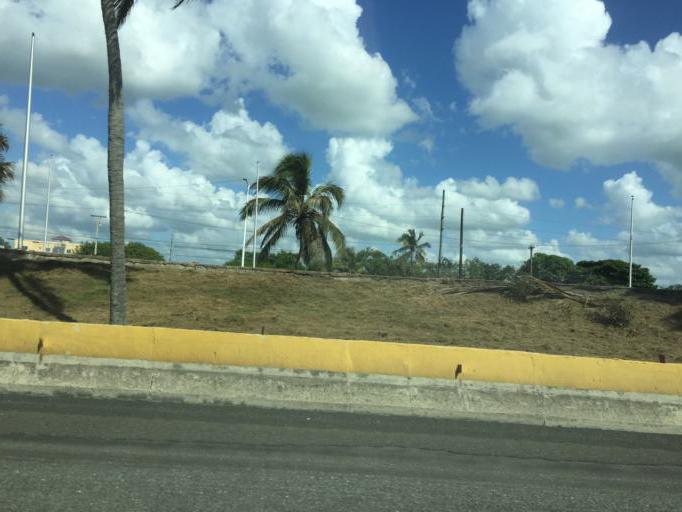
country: DO
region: Santo Domingo
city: Guerra
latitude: 18.4562
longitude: -69.7152
